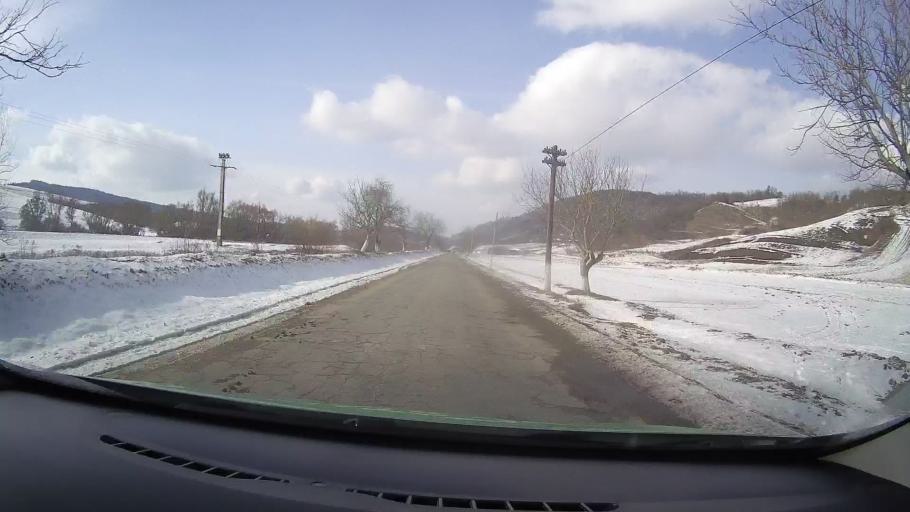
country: RO
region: Sibiu
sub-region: Comuna Iacobeni
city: Iacobeni
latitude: 46.0409
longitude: 24.7307
